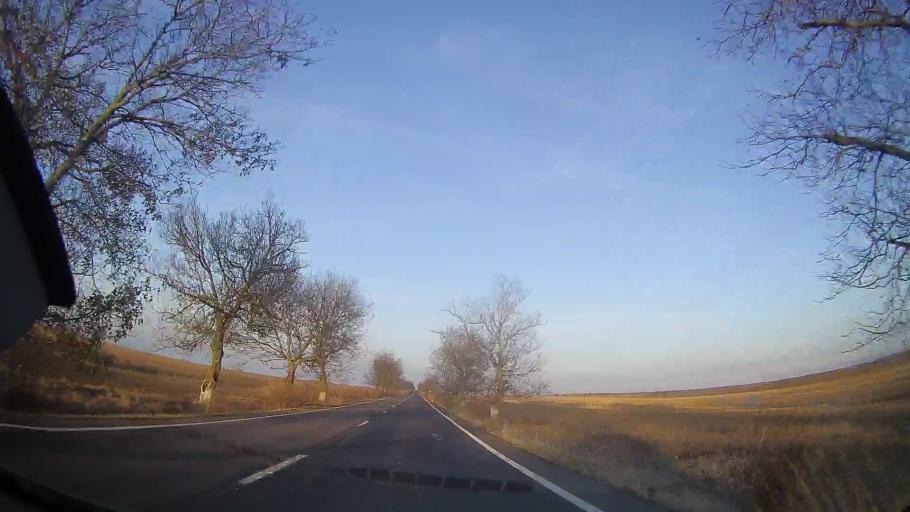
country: RO
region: Constanta
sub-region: Comuna Amzacea
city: Amzacea
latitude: 43.9345
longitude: 28.3640
